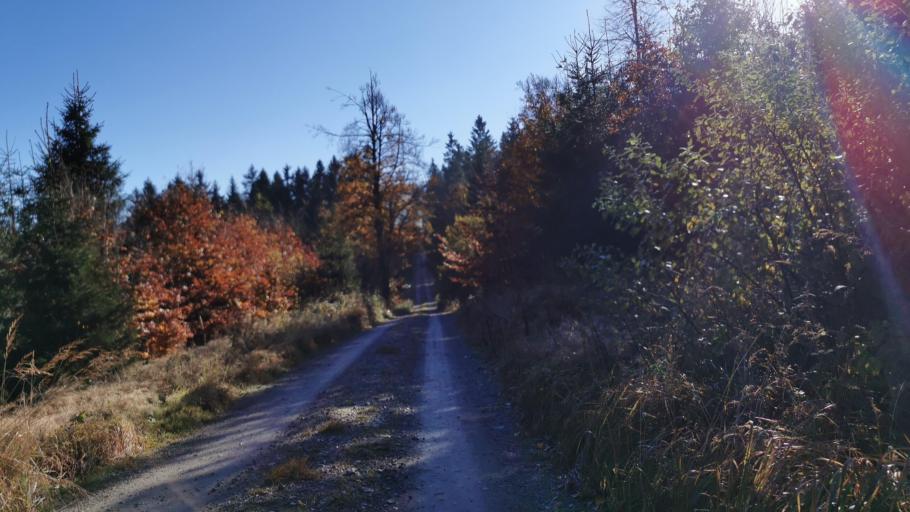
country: DE
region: Thuringia
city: Wurzbach
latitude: 50.4293
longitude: 11.5100
